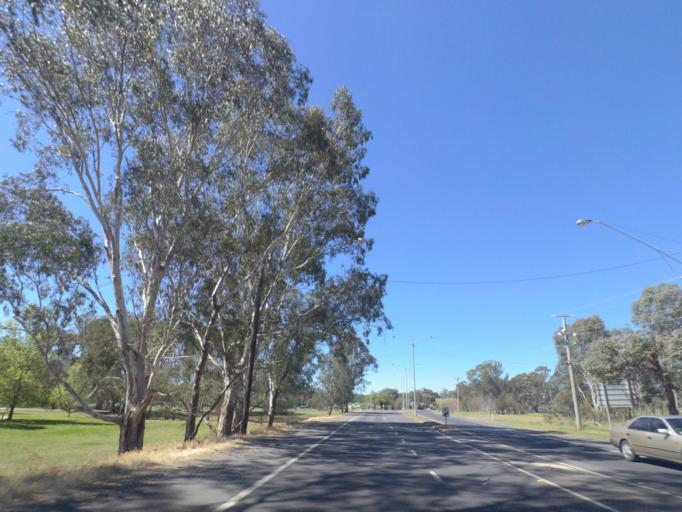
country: AU
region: Victoria
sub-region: Murrindindi
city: Kinglake West
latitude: -37.0230
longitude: 145.1148
